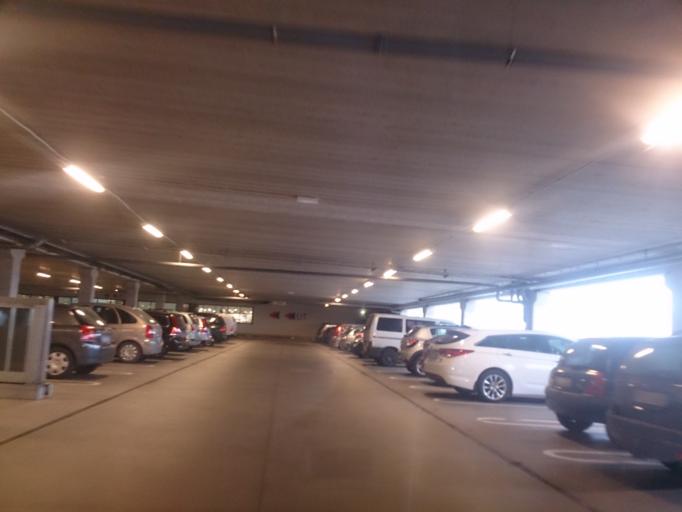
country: SE
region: OEstergoetland
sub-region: Norrkopings Kommun
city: Norrkoping
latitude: 58.5729
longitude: 16.2087
